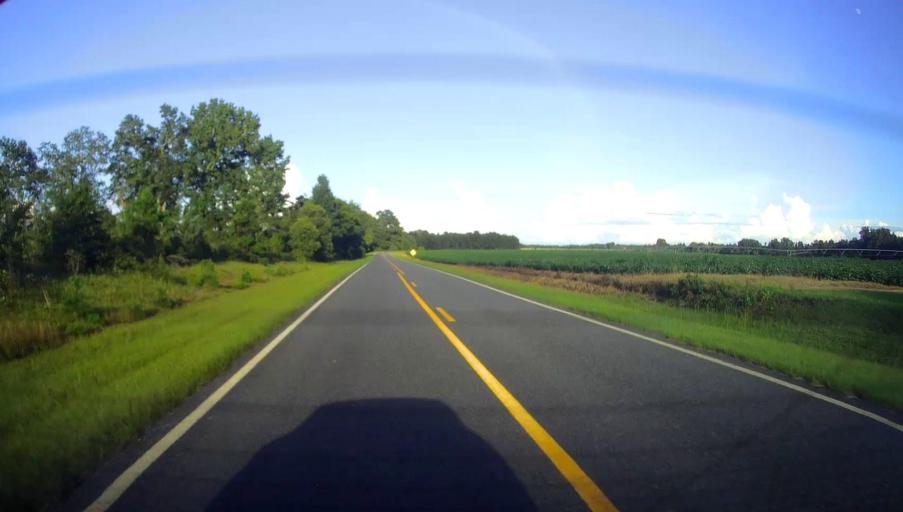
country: US
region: Georgia
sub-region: Pulaski County
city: Hawkinsville
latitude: 32.2877
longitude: -83.5493
